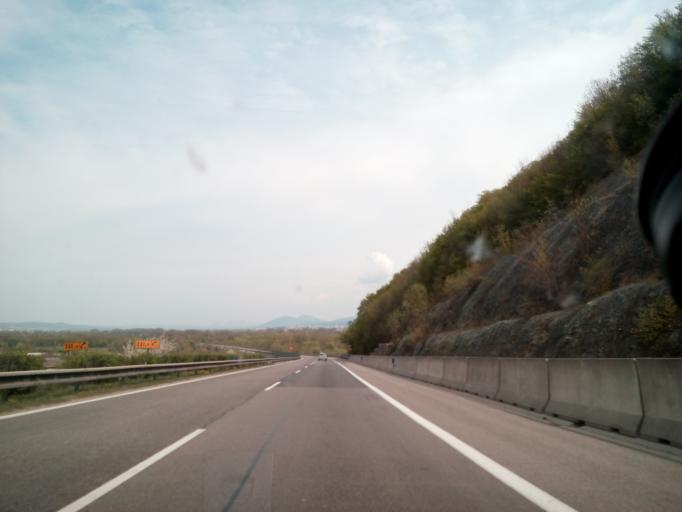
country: SK
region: Trenciansky
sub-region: Okres Trencin
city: Trencin
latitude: 48.9213
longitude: 18.0719
